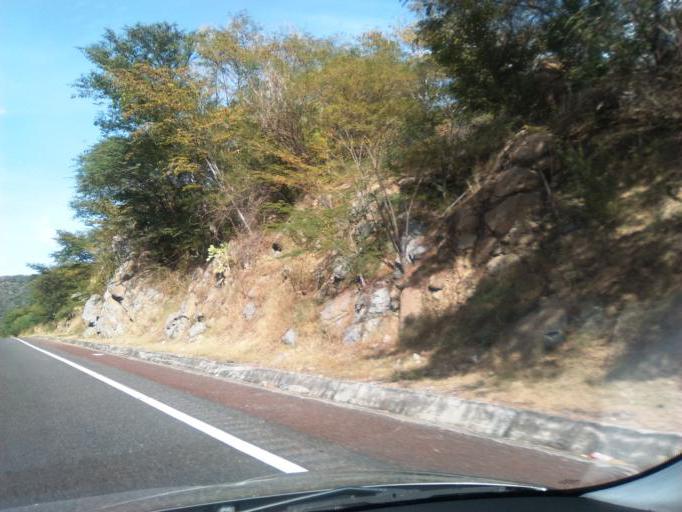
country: MX
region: Guerrero
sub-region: Huitzuco de los Figueroa
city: Ciudad de Huitzuco
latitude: 18.3528
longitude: -99.1840
